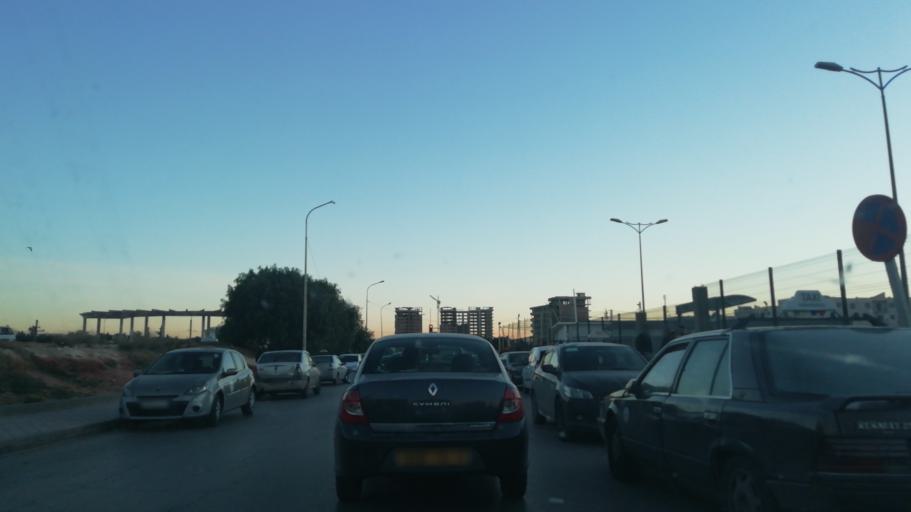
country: DZ
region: Oran
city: Bir el Djir
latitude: 35.7033
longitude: -0.5909
